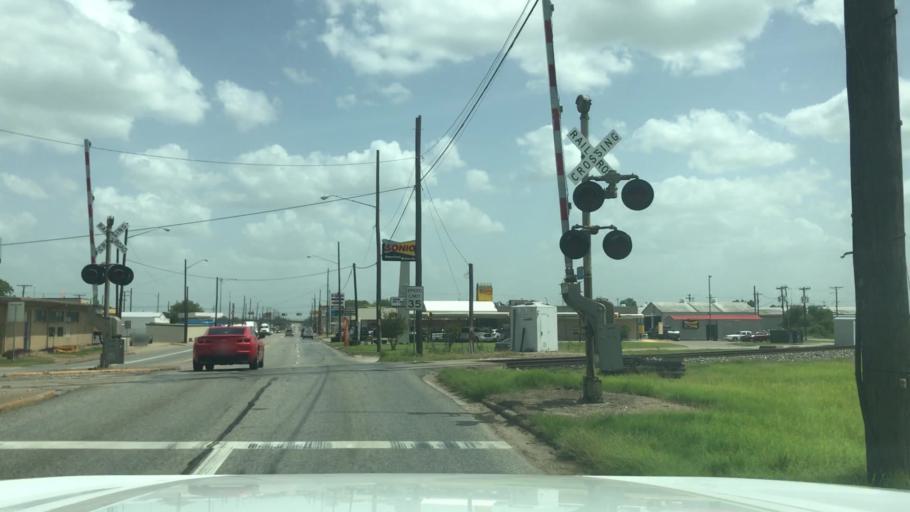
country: US
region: Texas
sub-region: Robertson County
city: Hearne
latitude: 30.8844
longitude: -96.5974
